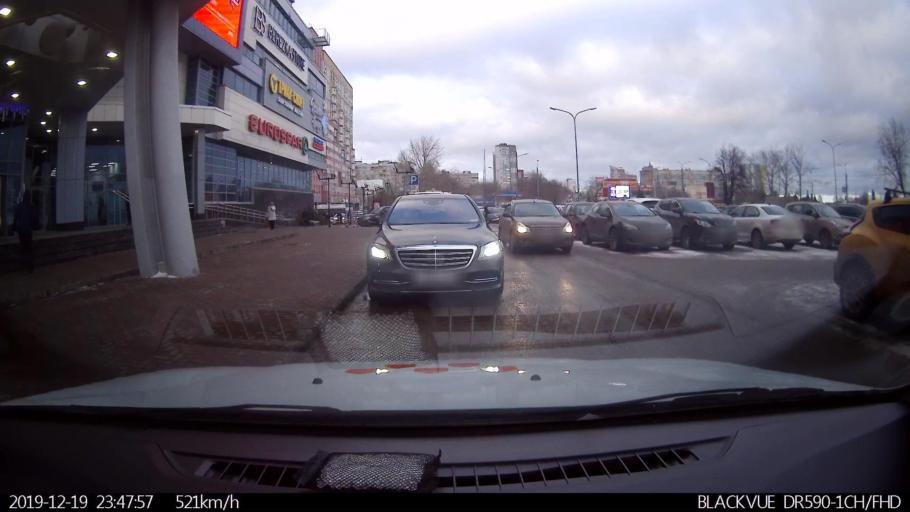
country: RU
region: Tverskaya
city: Ves'yegonsk
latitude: 58.7090
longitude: 37.5878
